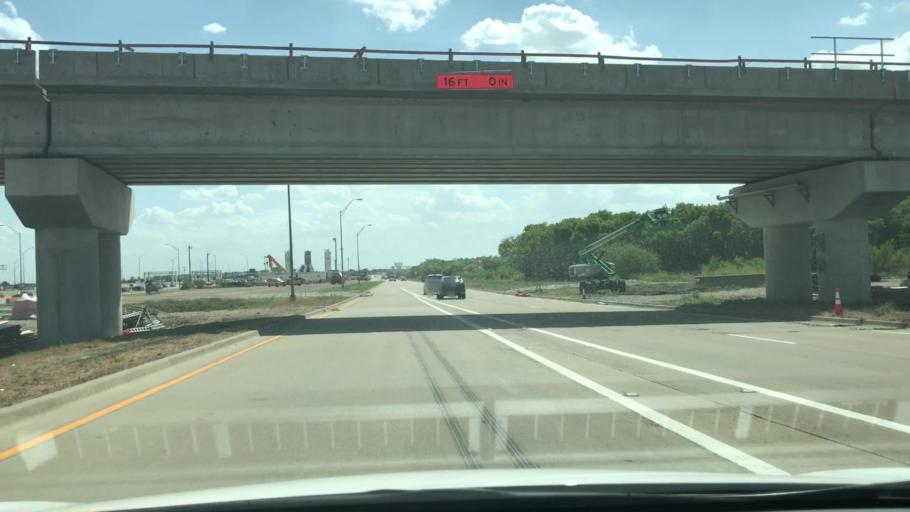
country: US
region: Texas
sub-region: Tarrant County
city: Grapevine
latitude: 32.9302
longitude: -97.0504
